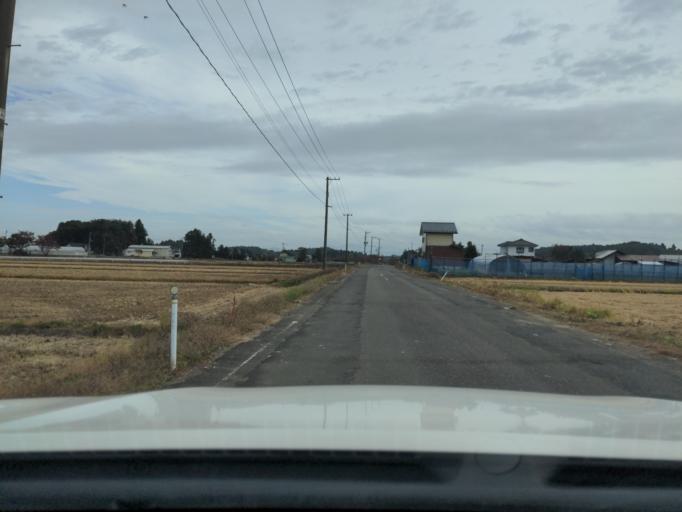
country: JP
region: Fukushima
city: Koriyama
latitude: 37.3463
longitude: 140.2968
